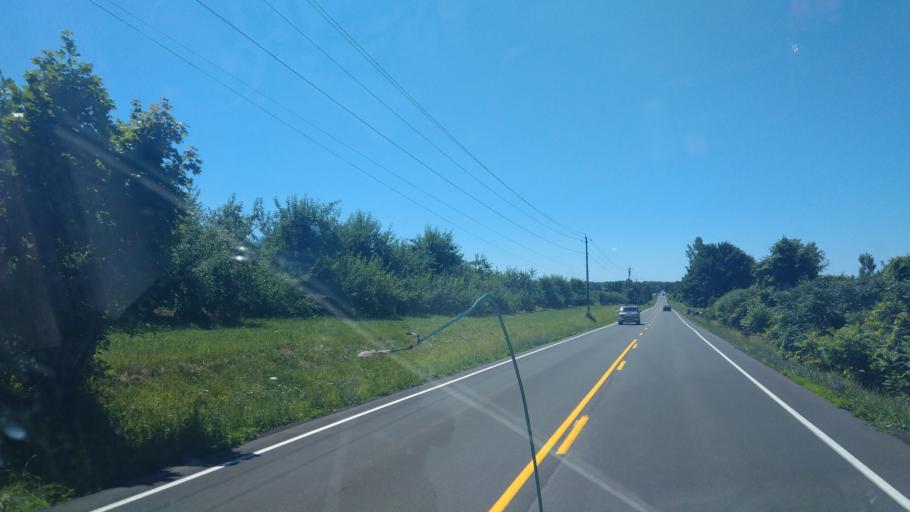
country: US
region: New York
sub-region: Wayne County
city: Sodus
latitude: 43.2331
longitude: -76.9824
